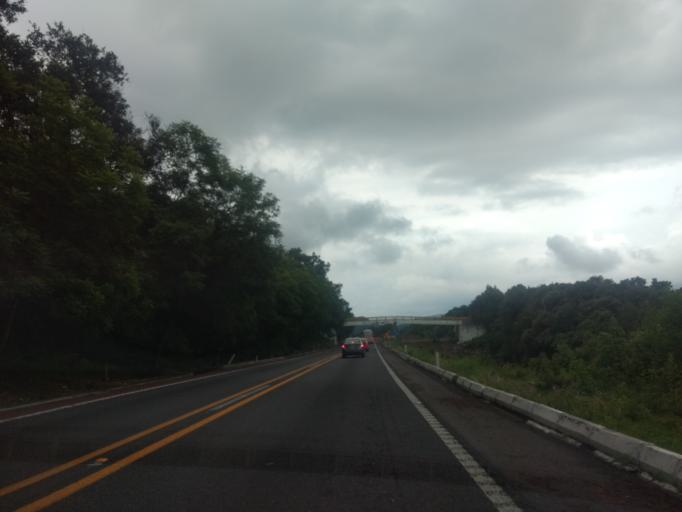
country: MX
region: Morelos
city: Tepoztlan
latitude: 18.9946
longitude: -99.1213
